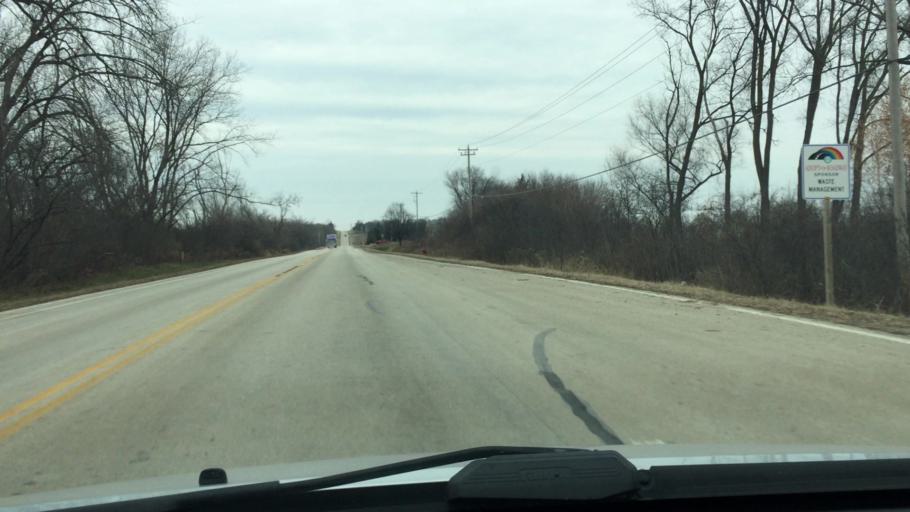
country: US
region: Wisconsin
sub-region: Waukesha County
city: Menomonee Falls
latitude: 43.1942
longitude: -88.0634
